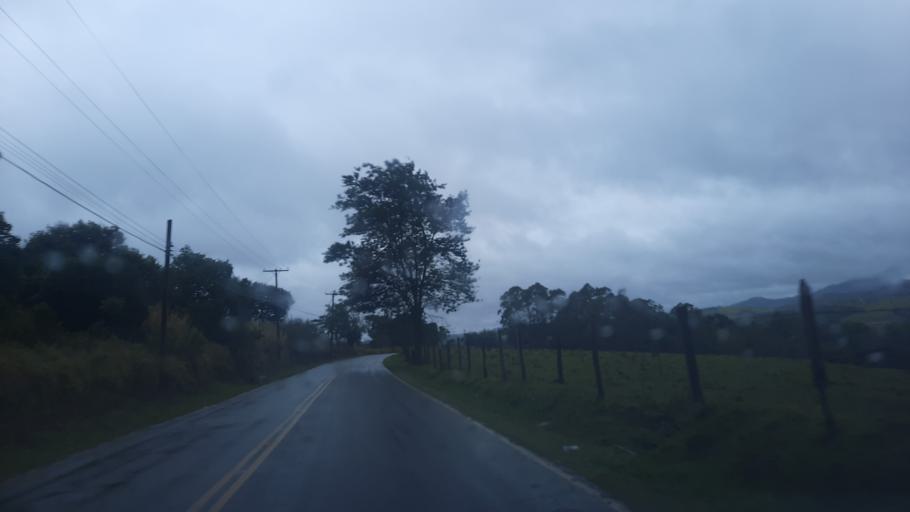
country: BR
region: Sao Paulo
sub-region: Atibaia
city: Atibaia
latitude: -23.0739
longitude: -46.5185
